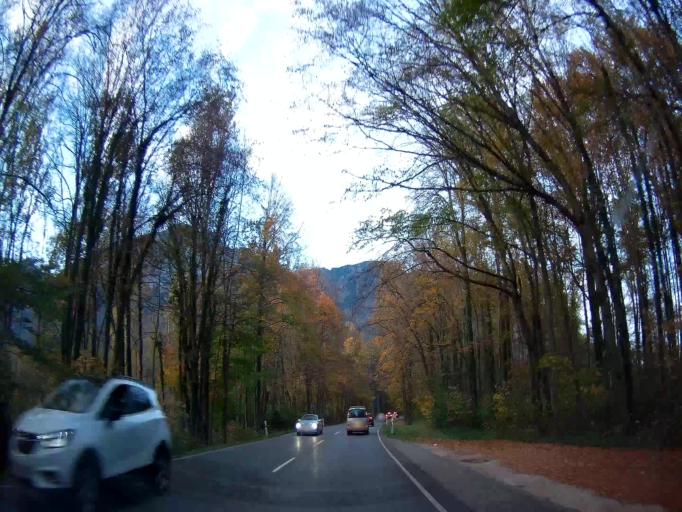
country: DE
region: Bavaria
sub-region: Upper Bavaria
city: Bad Reichenhall
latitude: 47.7262
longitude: 12.8662
